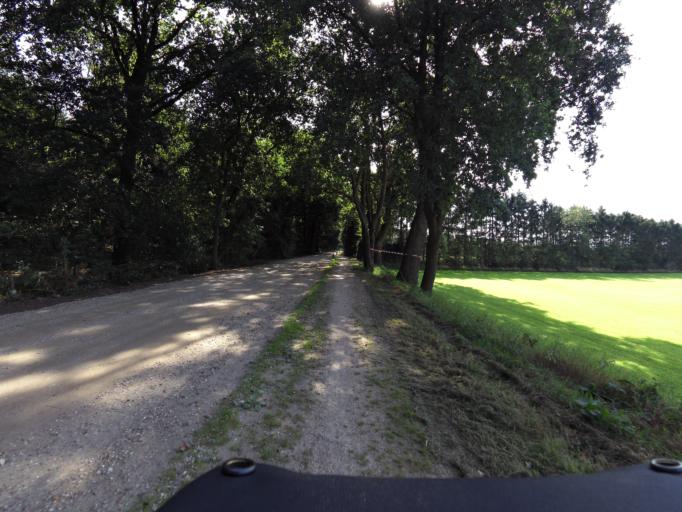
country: NL
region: Gelderland
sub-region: Gemeente Apeldoorn
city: Uddel
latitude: 52.2172
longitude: 5.7698
